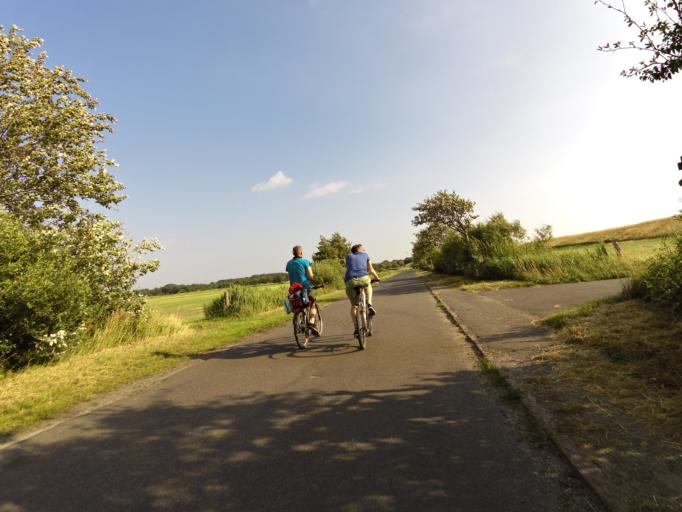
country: DE
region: Lower Saxony
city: Nordholz
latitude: 53.8333
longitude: 8.5804
